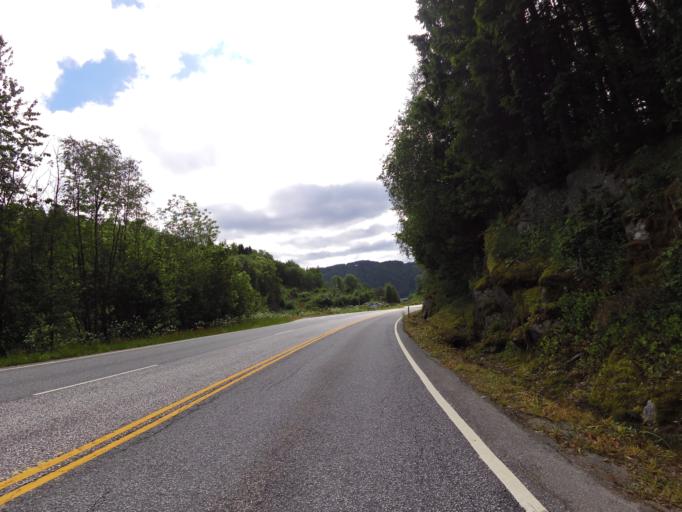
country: NO
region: Vest-Agder
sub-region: Flekkefjord
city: Flekkefjord
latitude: 58.2661
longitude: 6.8069
